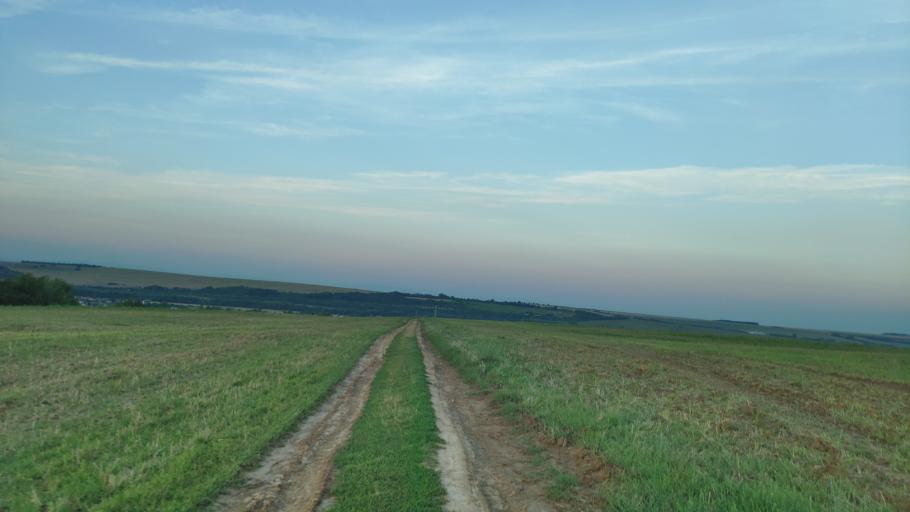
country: SK
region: Kosicky
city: Secovce
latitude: 48.5937
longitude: 21.5445
